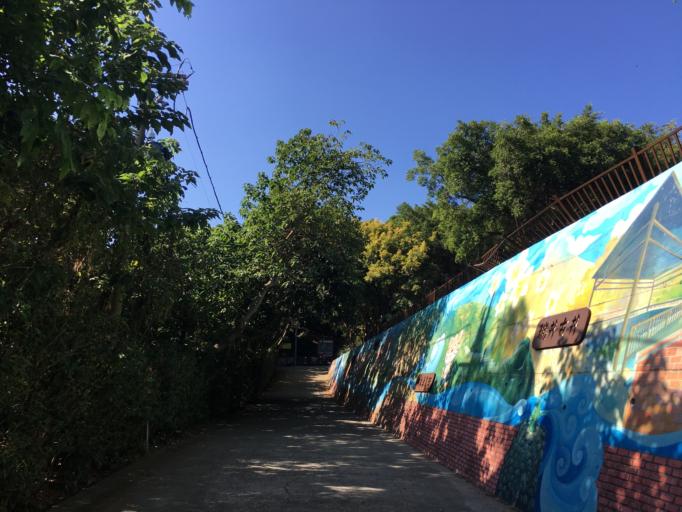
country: TW
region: Taiwan
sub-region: Changhua
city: Chang-hua
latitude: 24.1448
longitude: 120.5574
